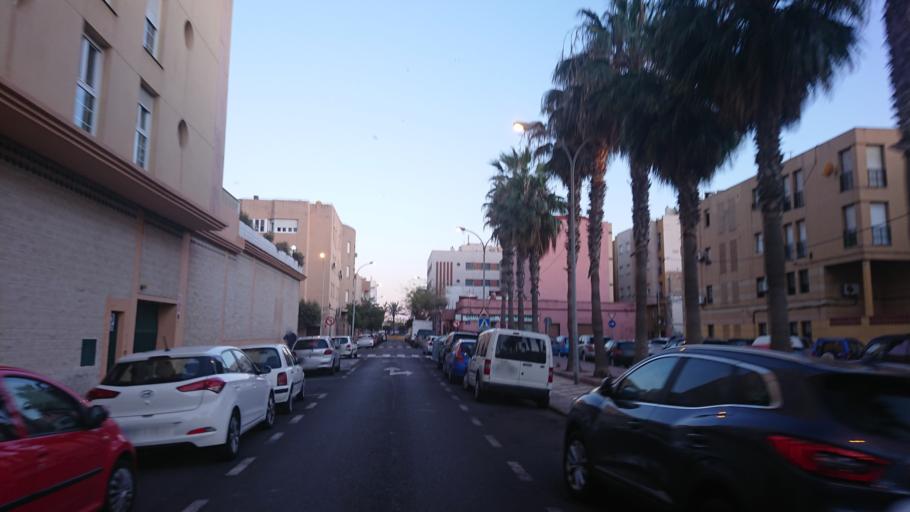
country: ES
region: Melilla
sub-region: Melilla
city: Melilla
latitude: 35.2795
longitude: -2.9373
